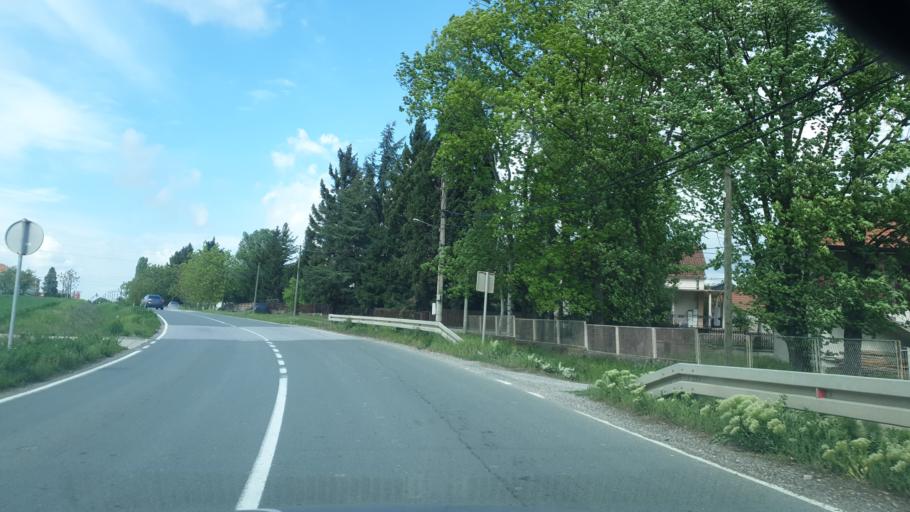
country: RS
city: Stubline
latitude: 44.5544
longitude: 20.1468
